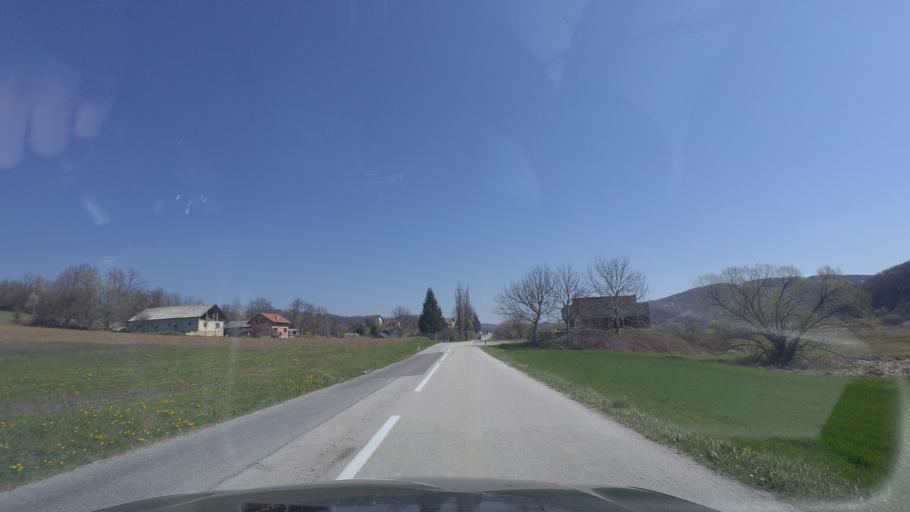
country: HR
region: Karlovacka
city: Vojnic
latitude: 45.3771
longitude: 15.6238
